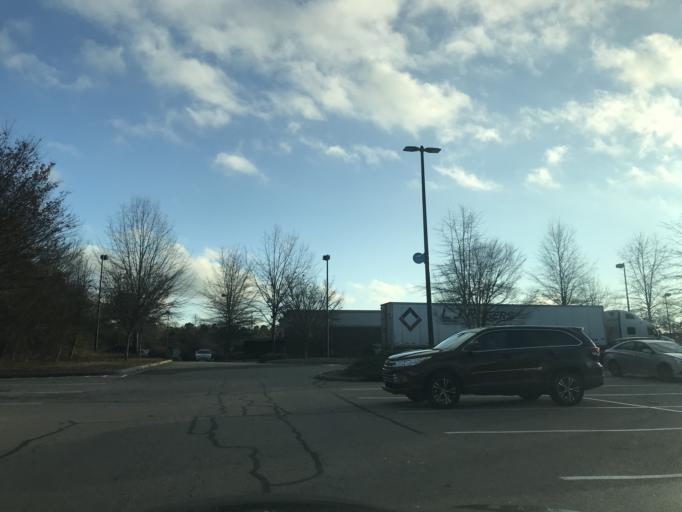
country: US
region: North Carolina
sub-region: Wake County
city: Wake Forest
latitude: 35.9504
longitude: -78.5340
